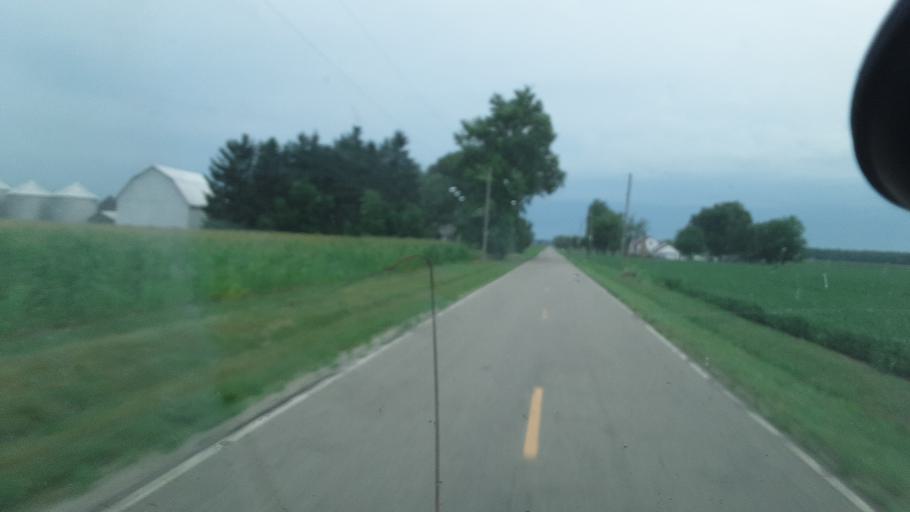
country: US
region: Ohio
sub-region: Defiance County
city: Hicksville
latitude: 41.2670
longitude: -84.7439
